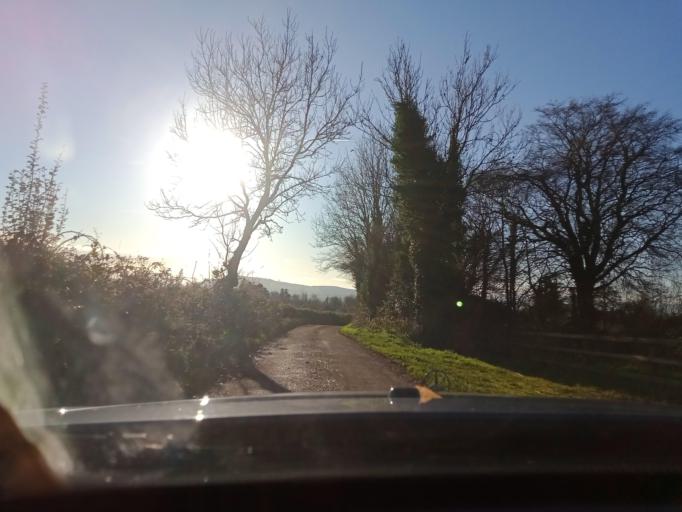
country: IE
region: Leinster
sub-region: Kilkenny
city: Callan
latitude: 52.4583
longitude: -7.4236
